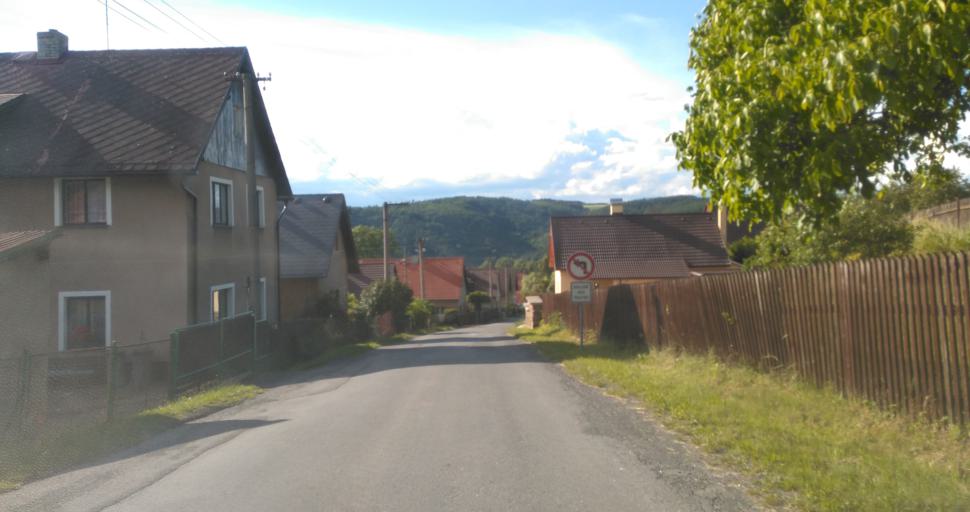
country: CZ
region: Central Bohemia
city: Roztoky
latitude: 50.0084
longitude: 13.8463
